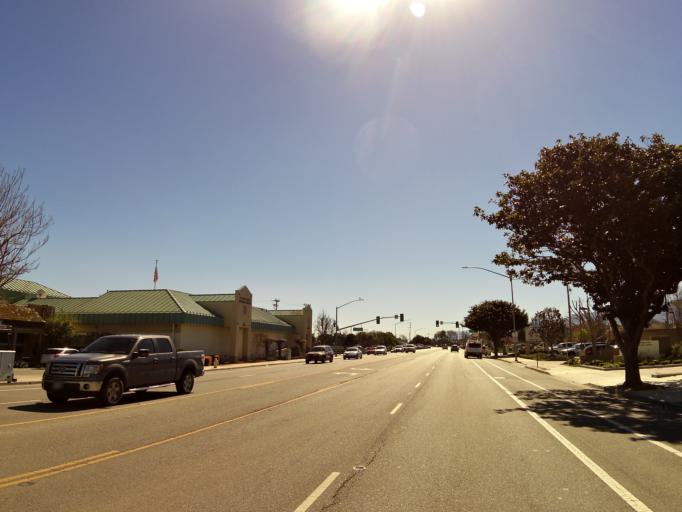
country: US
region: California
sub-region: Monterey County
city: Salinas
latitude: 36.6633
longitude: -121.6423
